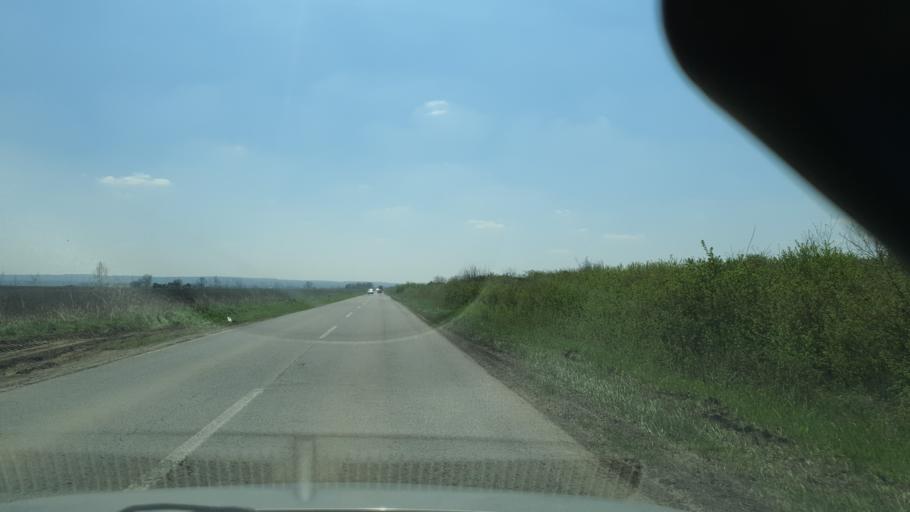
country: RS
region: Autonomna Pokrajina Vojvodina
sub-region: Juznobacki Okrug
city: Backa Palanka
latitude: 45.3030
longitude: 19.4352
